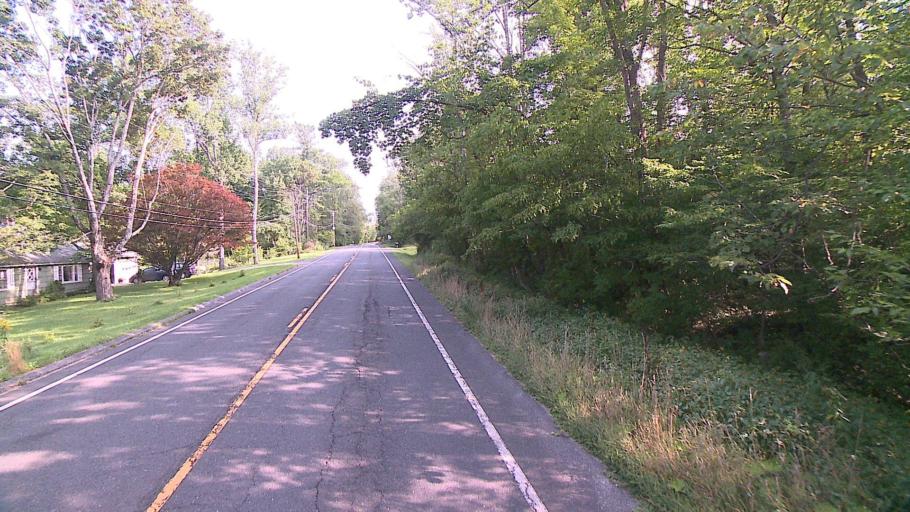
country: US
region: Connecticut
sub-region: Litchfield County
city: Canaan
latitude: 41.9488
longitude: -73.3598
